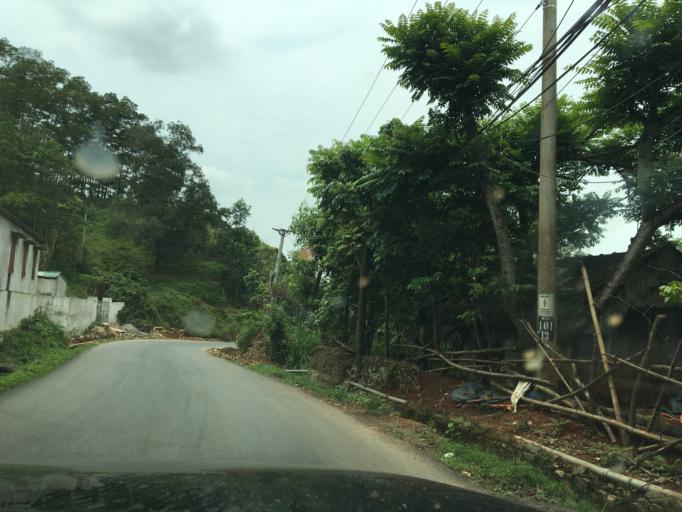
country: VN
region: Ninh Binh
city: Thi Tran Nho Quan
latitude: 20.2169
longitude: 105.7983
